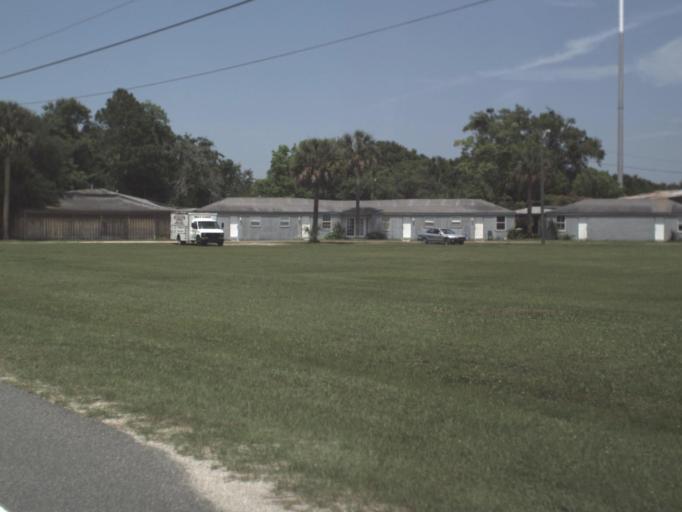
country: US
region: Florida
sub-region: Nassau County
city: Yulee
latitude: 30.5095
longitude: -81.6228
